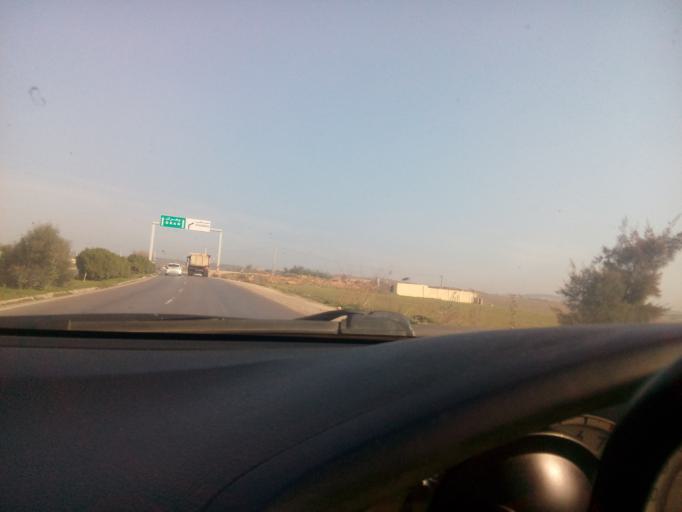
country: DZ
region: Oran
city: Es Senia
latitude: 35.6226
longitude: -0.7184
